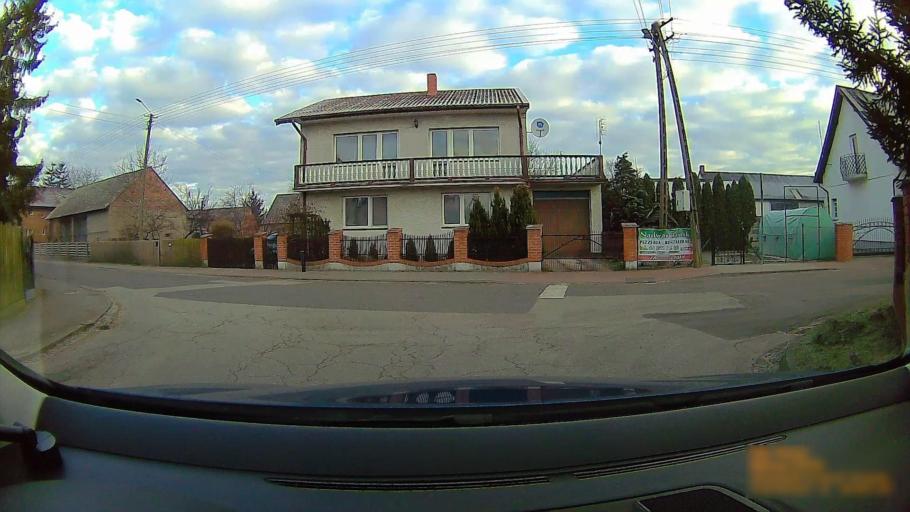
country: PL
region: Greater Poland Voivodeship
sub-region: Powiat koninski
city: Rzgow Pierwszy
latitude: 52.1532
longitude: 18.0519
